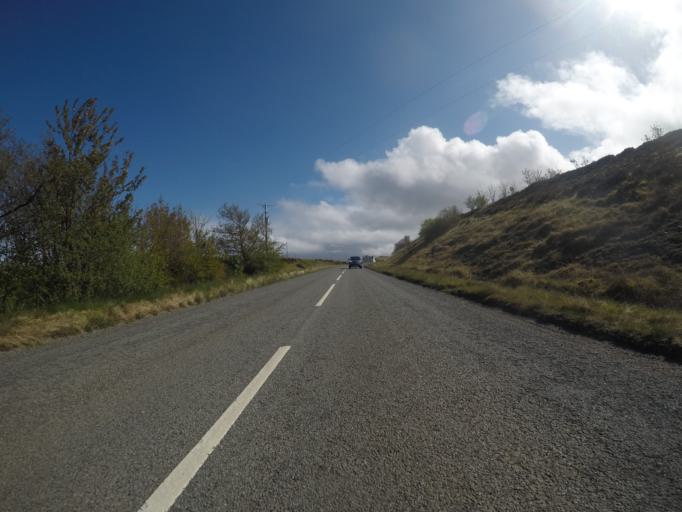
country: GB
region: Scotland
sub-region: Highland
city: Portree
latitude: 57.5768
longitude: -6.1559
